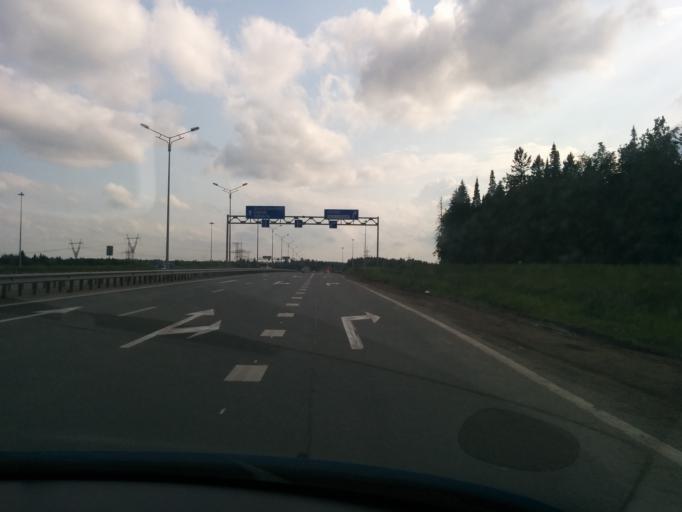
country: RU
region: Perm
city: Ferma
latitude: 58.0023
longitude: 56.3901
